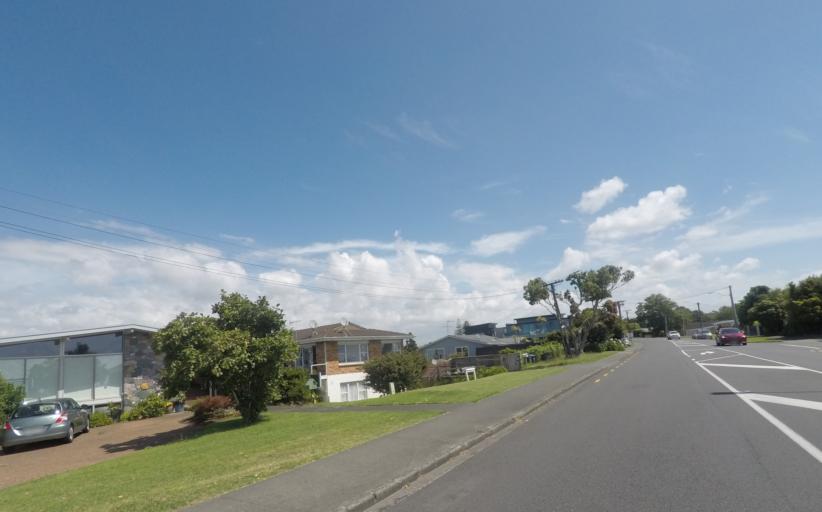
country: NZ
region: Auckland
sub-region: Auckland
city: Tamaki
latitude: -36.8718
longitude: 174.8445
